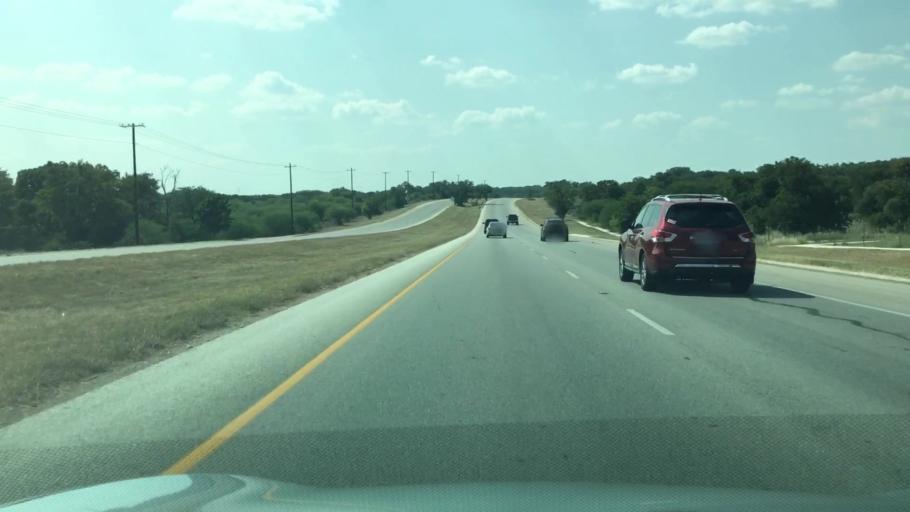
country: US
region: Texas
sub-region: Hays County
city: San Marcos
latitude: 29.8819
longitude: -97.9734
